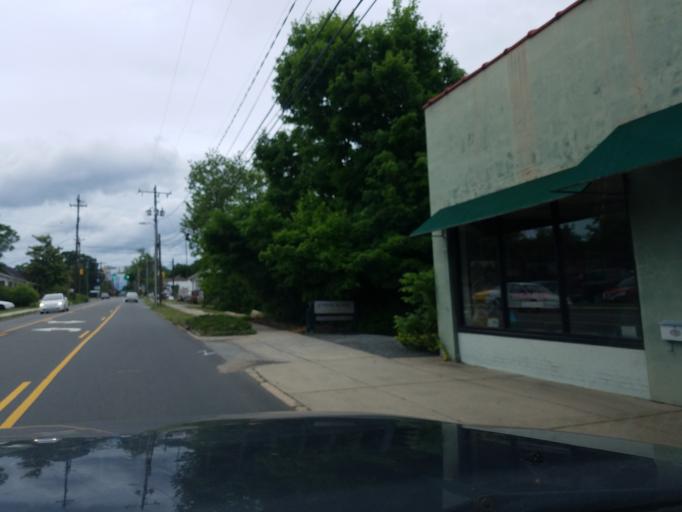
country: US
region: North Carolina
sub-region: Durham County
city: Durham
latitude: 36.0110
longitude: -78.9291
